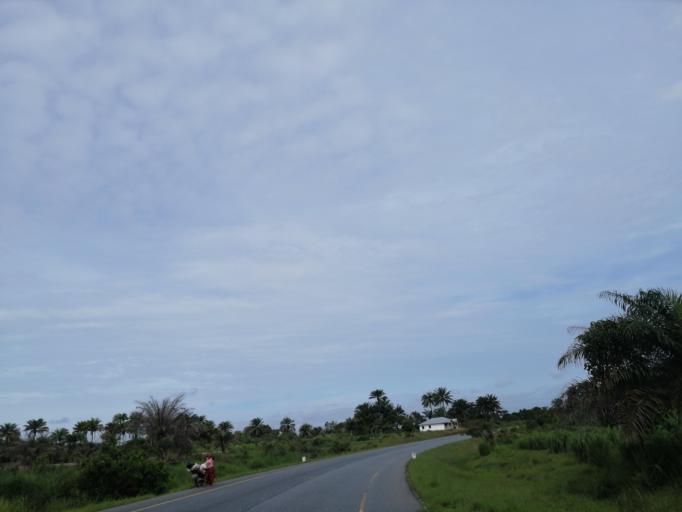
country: SL
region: Northern Province
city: Port Loko
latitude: 8.7665
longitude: -12.8871
